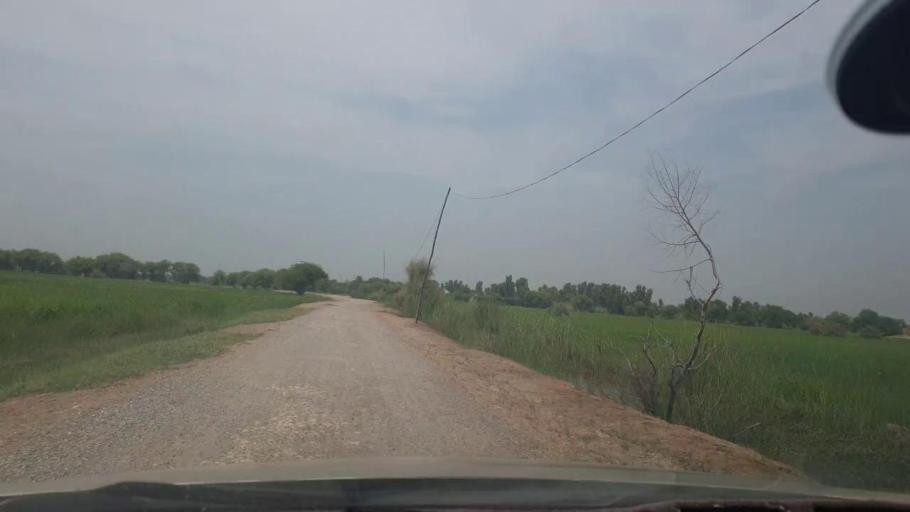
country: PK
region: Sindh
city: Jacobabad
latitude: 28.2418
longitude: 68.4323
